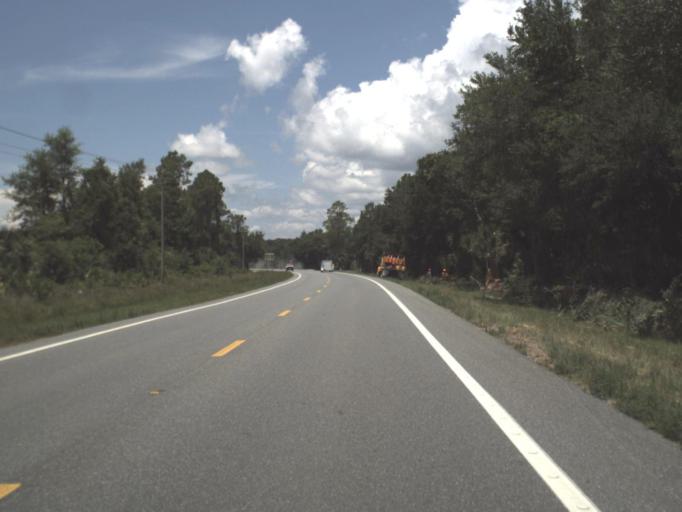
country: US
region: Florida
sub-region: Leon County
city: Woodville
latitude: 30.1437
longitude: -83.9414
